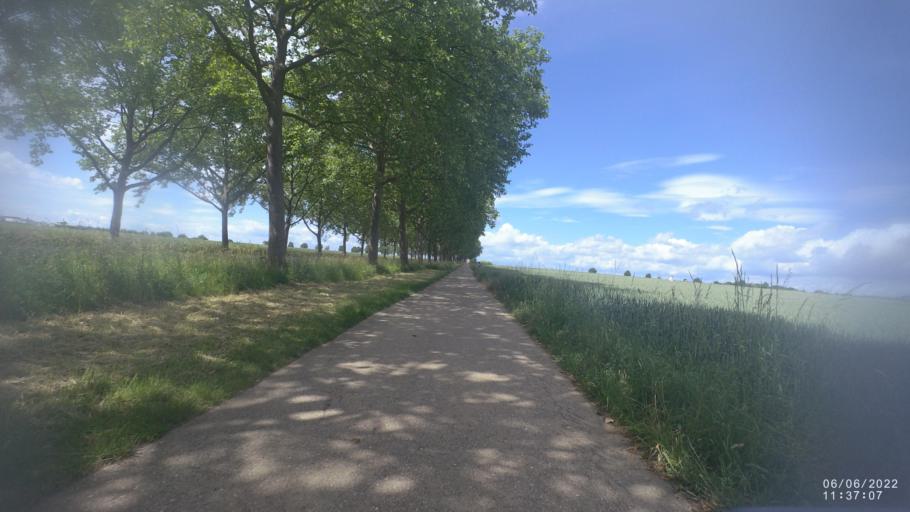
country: DE
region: Baden-Wuerttemberg
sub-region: Regierungsbezirk Stuttgart
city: Fellbach
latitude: 48.8242
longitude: 9.2636
